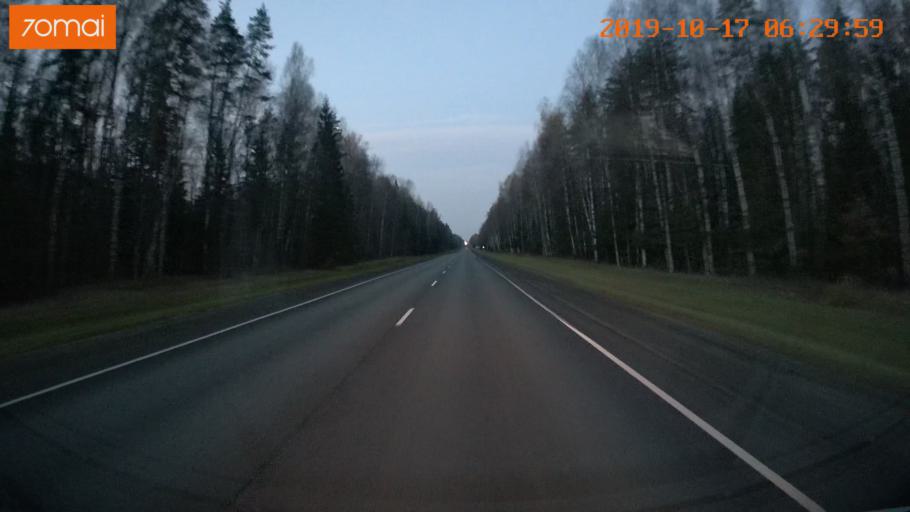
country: RU
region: Ivanovo
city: Lezhnevo
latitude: 56.7404
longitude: 40.7311
